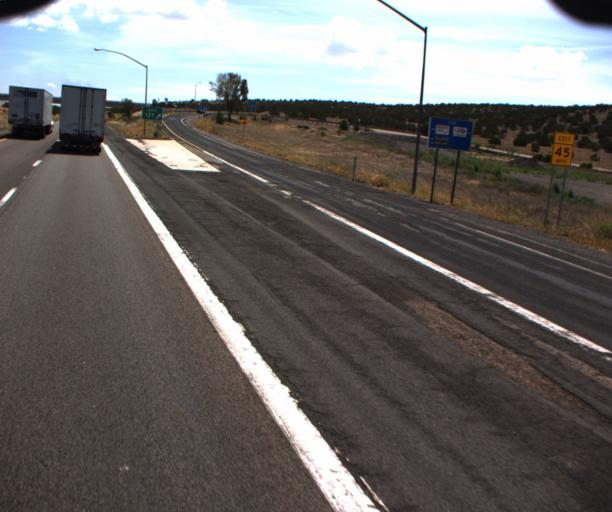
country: US
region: Arizona
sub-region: Mohave County
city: Peach Springs
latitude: 35.3205
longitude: -112.8960
